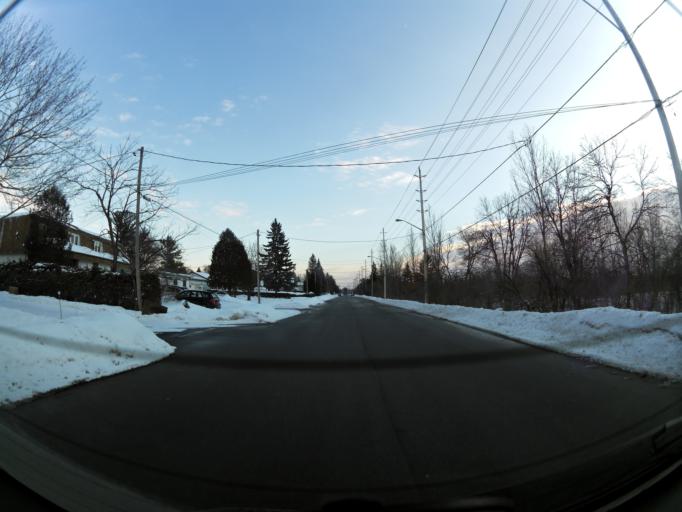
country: CA
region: Ontario
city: Ottawa
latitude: 45.4321
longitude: -75.5750
